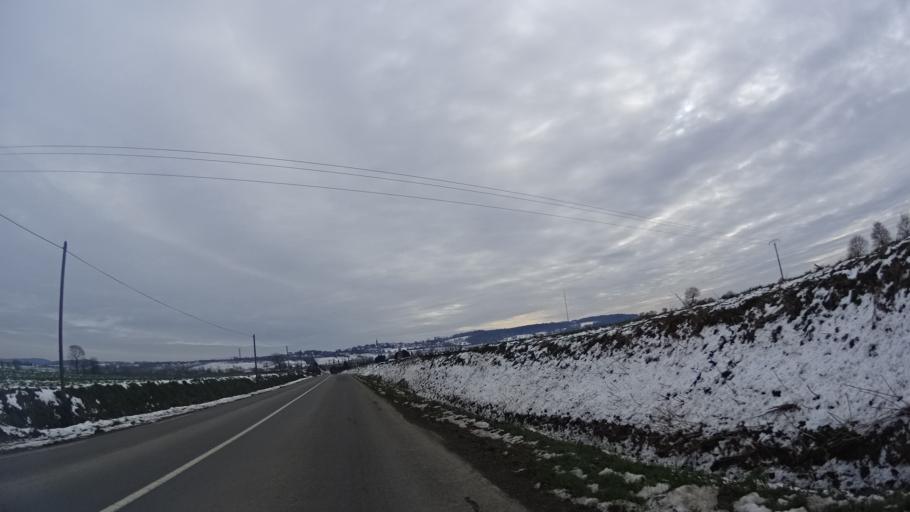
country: FR
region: Brittany
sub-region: Departement des Cotes-d'Armor
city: Plouasne
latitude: 48.3166
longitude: -1.9545
